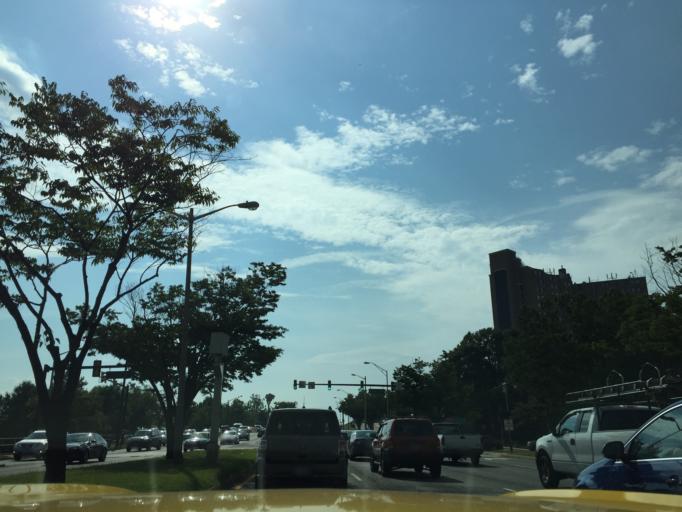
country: US
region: Virginia
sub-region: Fairfax County
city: Huntington
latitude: 38.8067
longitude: -77.0752
